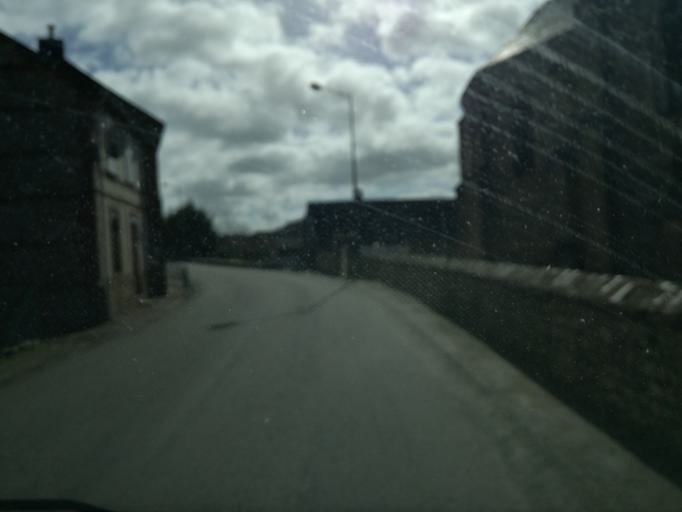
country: FR
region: Haute-Normandie
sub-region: Departement de la Seine-Maritime
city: Bretteville-du-Grand-Caux
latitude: 49.6950
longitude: 0.4767
